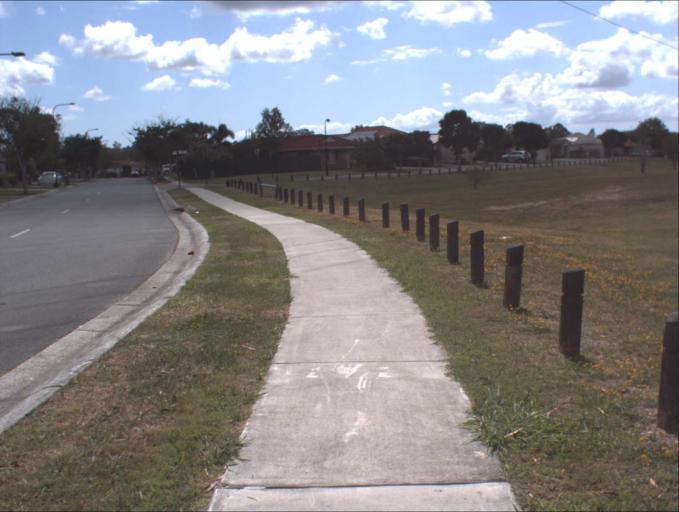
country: AU
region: Queensland
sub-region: Logan
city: Slacks Creek
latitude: -27.6596
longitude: 153.1446
